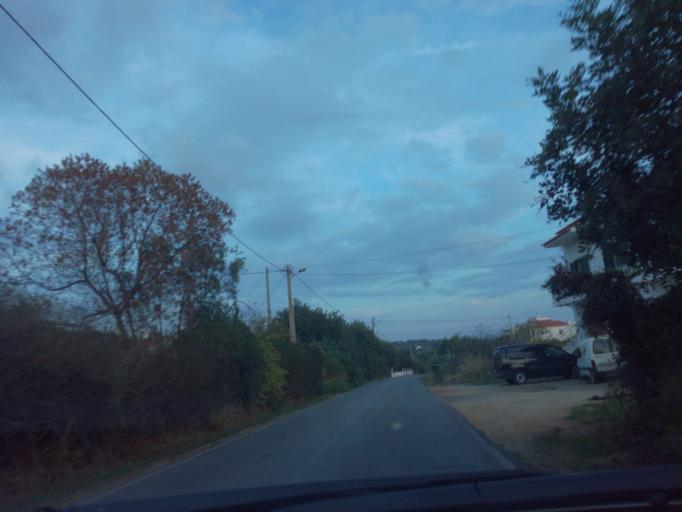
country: PT
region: Faro
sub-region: Sao Bras de Alportel
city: Sao Bras de Alportel
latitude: 37.0883
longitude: -7.8860
